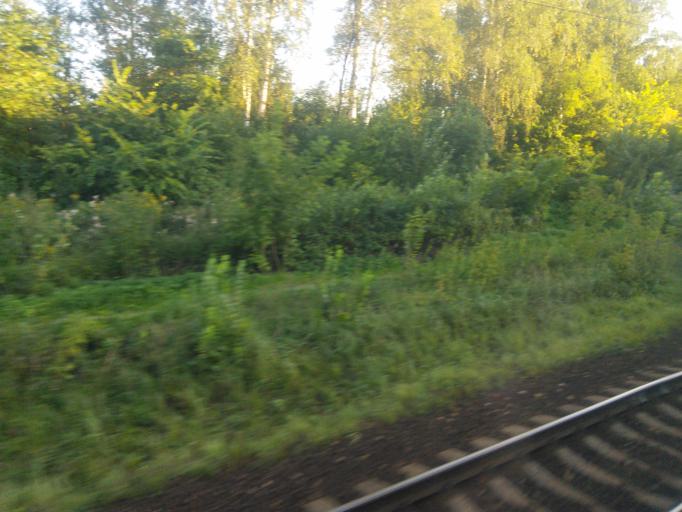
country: RU
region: Moskovskaya
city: Pavlovskiy Posad
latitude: 55.7688
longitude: 38.6272
